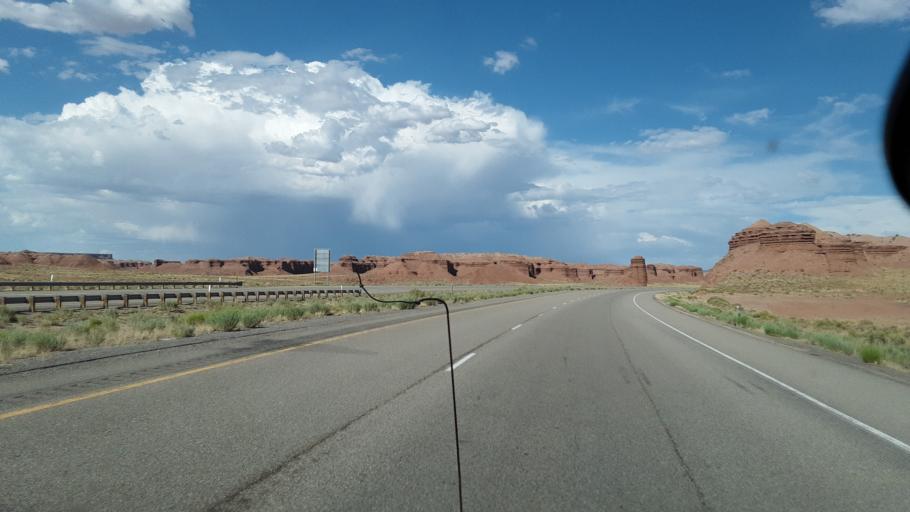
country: US
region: Utah
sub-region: Emery County
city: Ferron
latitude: 38.8430
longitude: -111.0593
